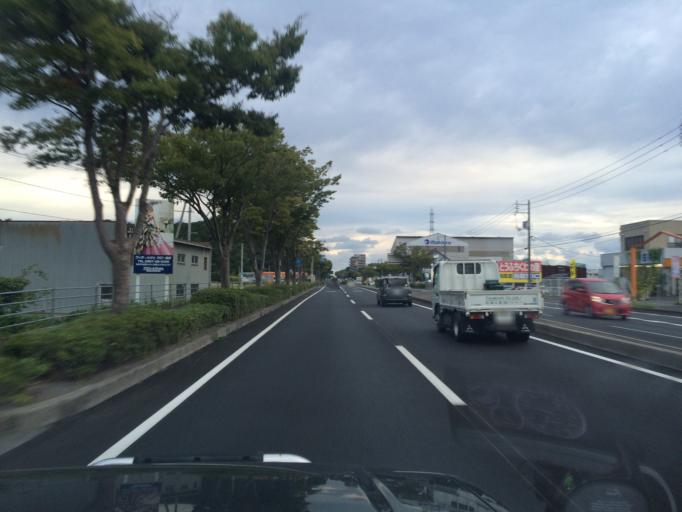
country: JP
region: Tottori
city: Tottori
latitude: 35.4916
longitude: 134.2036
